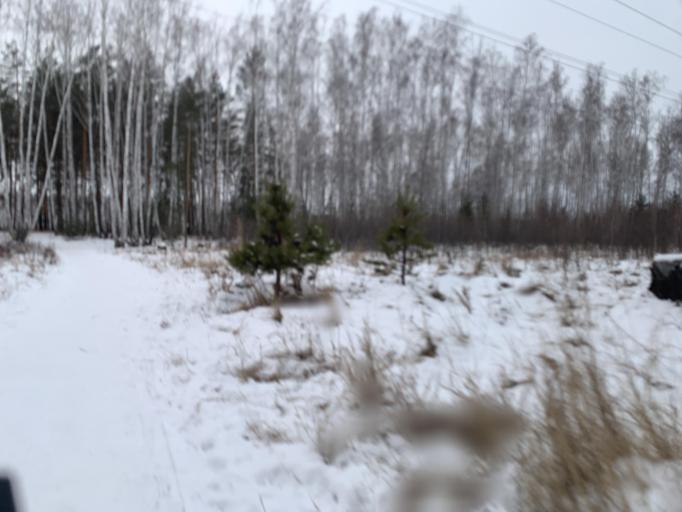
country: RU
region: Chelyabinsk
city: Roshchino
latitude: 55.2027
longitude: 61.2666
